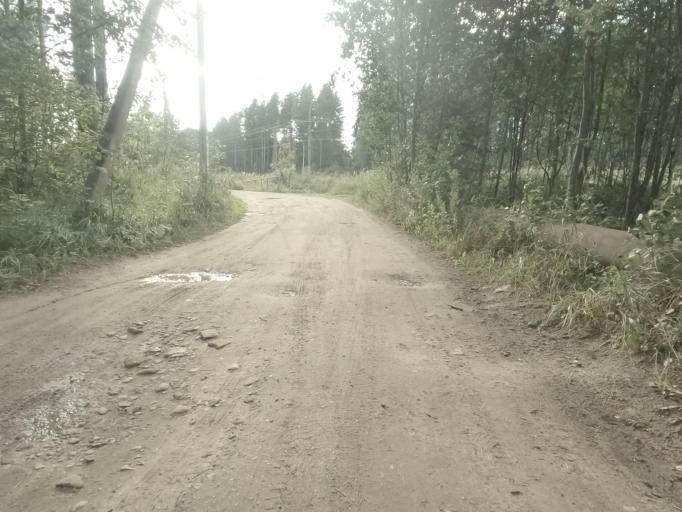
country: RU
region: Leningrad
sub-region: Volosovskiy Rayon
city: Shlissel'burg
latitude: 59.9472
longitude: 30.9894
